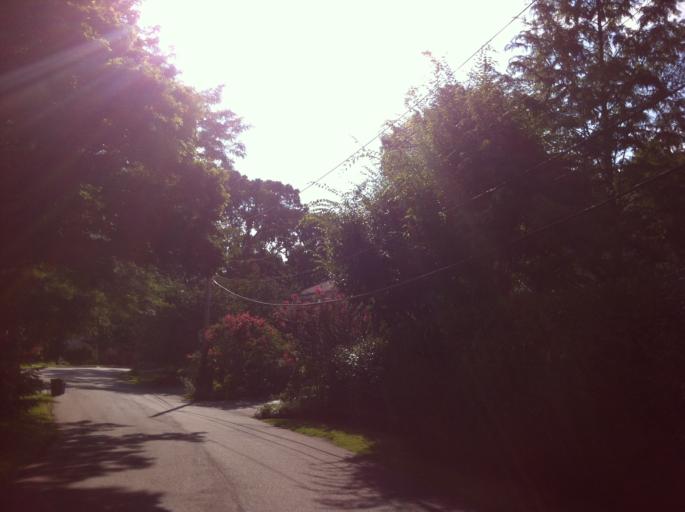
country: US
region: New York
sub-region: Nassau County
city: Sea Cliff
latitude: 40.8432
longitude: -73.6438
